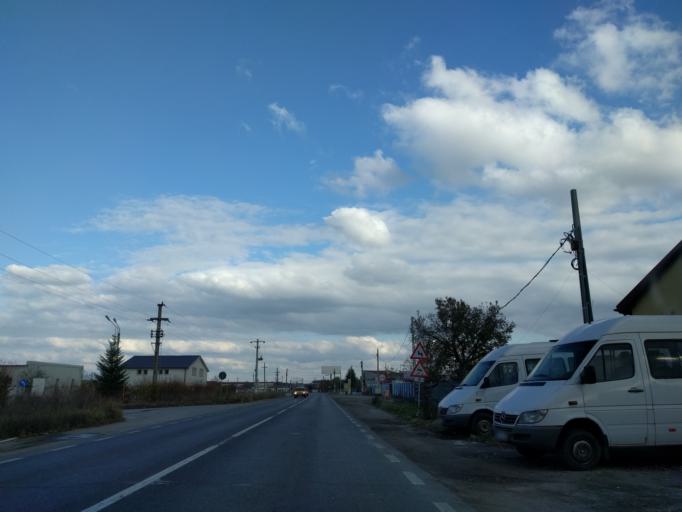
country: RO
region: Ilfov
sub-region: Comuna Ganeasa
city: Ganeasa
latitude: 44.4542
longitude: 26.2688
